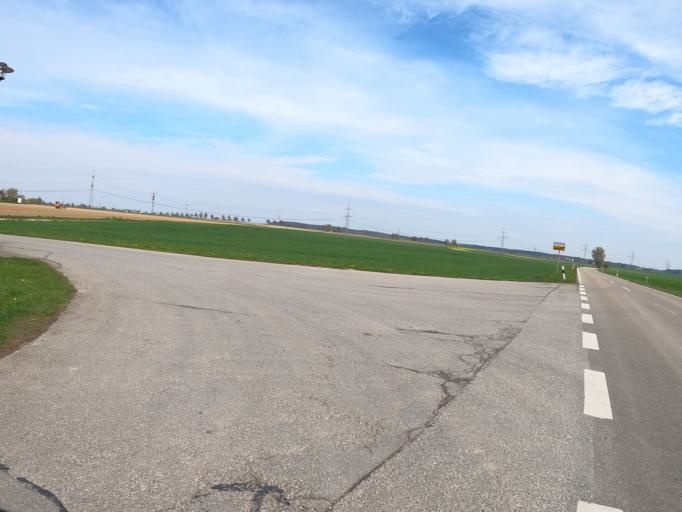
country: DE
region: Bavaria
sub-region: Swabia
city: Rieden an der Kotz
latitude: 48.3849
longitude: 10.2161
